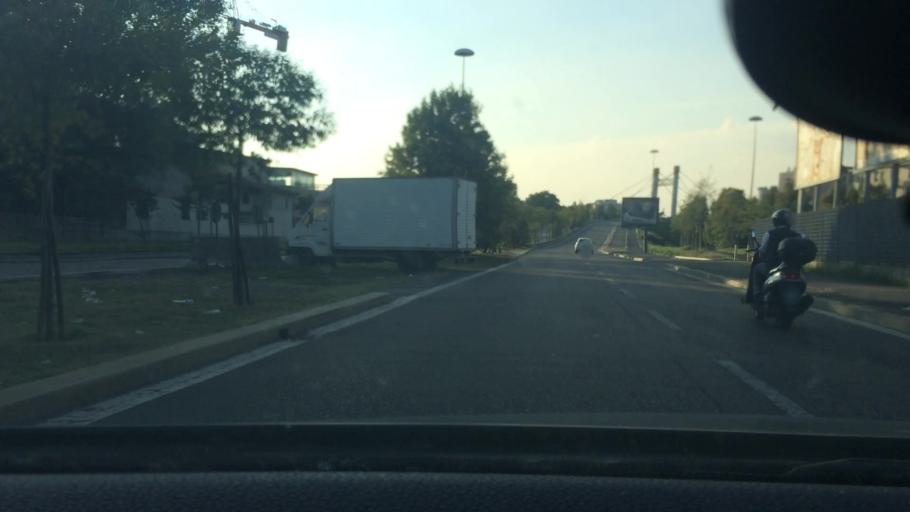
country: IT
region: Lombardy
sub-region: Citta metropolitana di Milano
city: Novate Milanese
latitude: 45.5027
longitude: 9.1428
